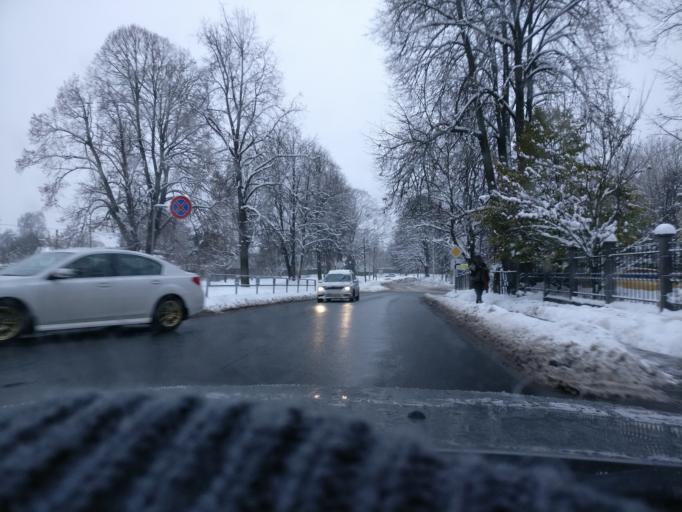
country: LV
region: Riga
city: Riga
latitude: 56.9273
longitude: 24.0799
